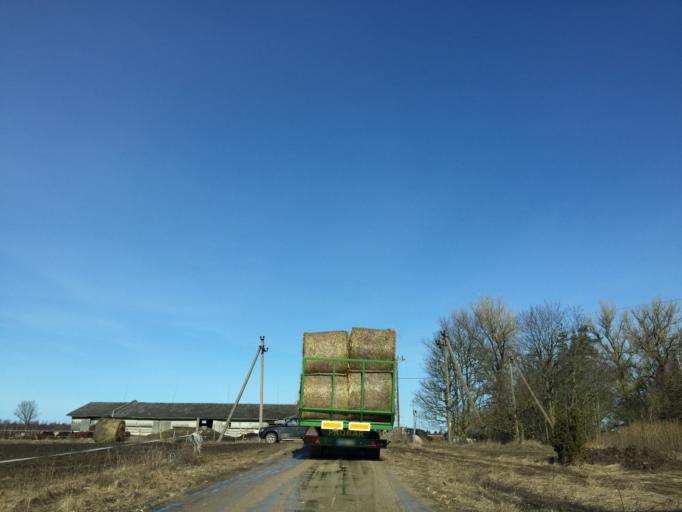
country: EE
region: Laeaene
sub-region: Haapsalu linn
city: Haapsalu
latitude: 58.6730
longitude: 23.5428
